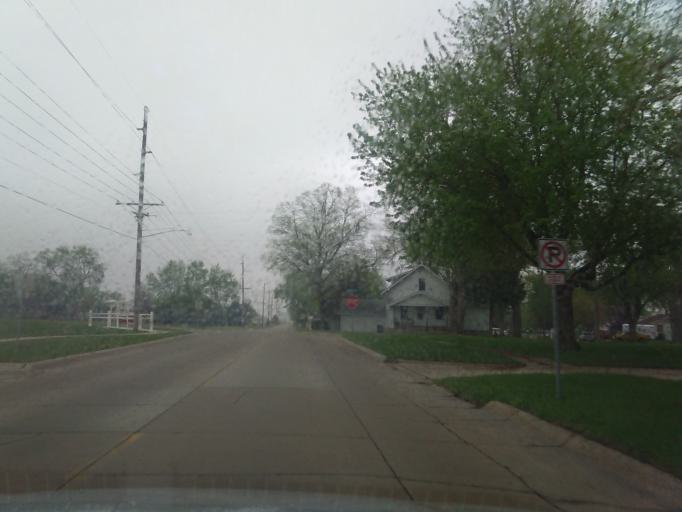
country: US
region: Nebraska
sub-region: Madison County
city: Norfolk
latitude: 42.0431
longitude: -97.4195
